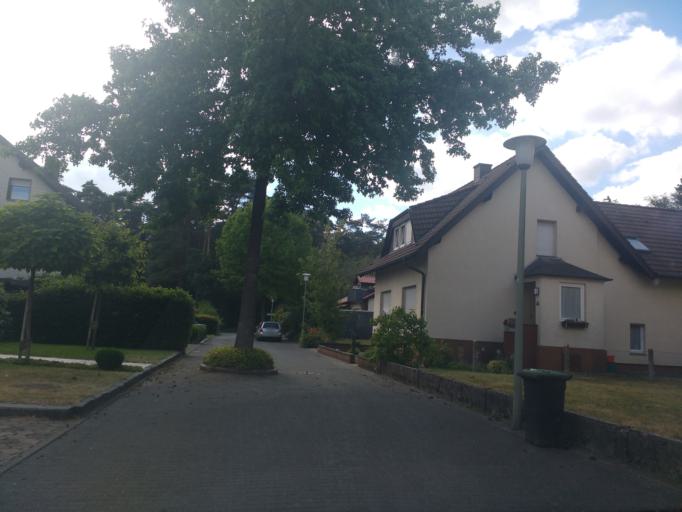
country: DE
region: North Rhine-Westphalia
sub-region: Regierungsbezirk Detmold
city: Schlangen
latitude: 51.7982
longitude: 8.8321
